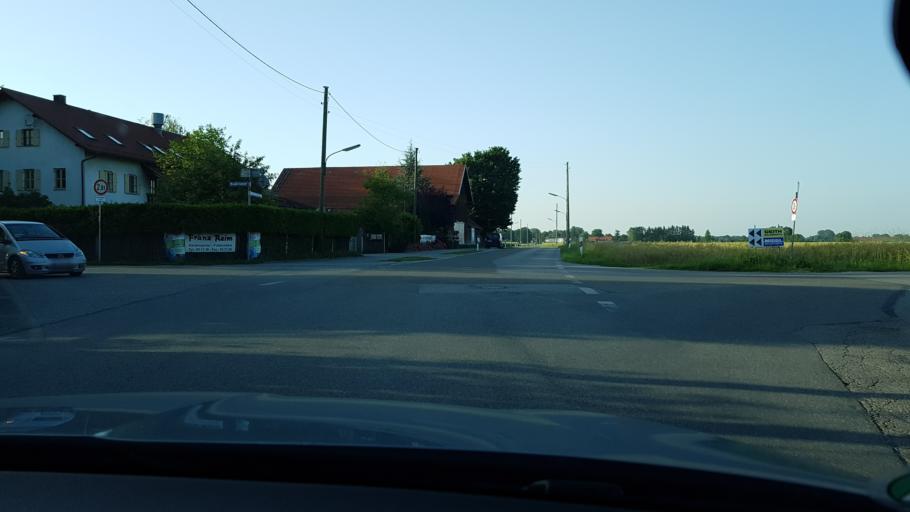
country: DE
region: Bavaria
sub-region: Upper Bavaria
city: Unterfoehring
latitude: 48.1534
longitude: 11.6587
